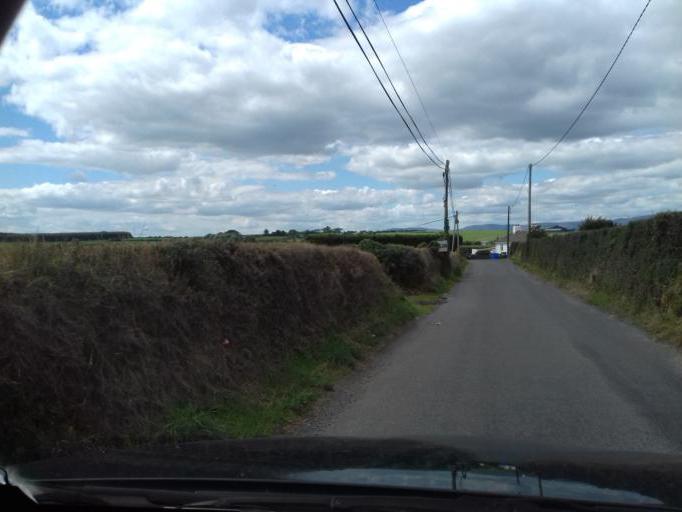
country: IE
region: Leinster
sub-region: Kilkenny
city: Mooncoin
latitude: 52.1740
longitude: -7.2747
